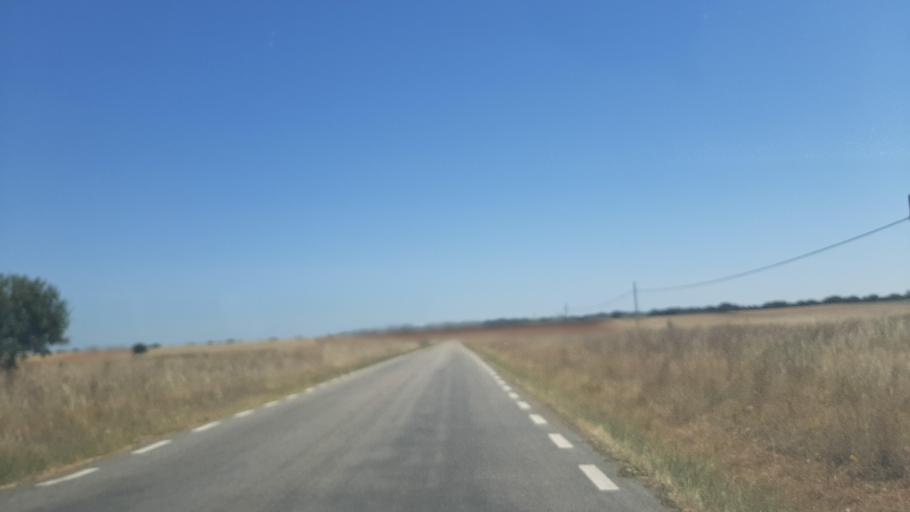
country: ES
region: Castille and Leon
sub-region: Provincia de Salamanca
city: Cabrillas
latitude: 40.7169
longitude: -6.1779
